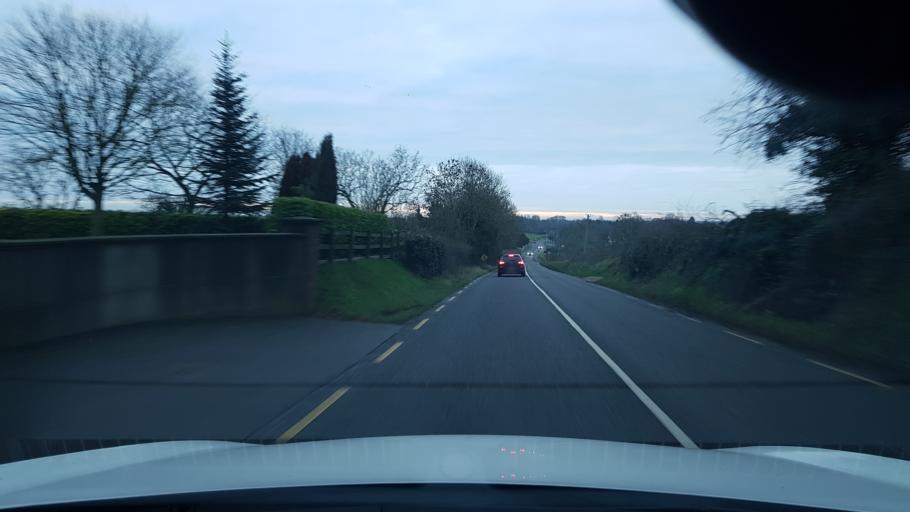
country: IE
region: Leinster
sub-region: An Mhi
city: Navan
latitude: 53.6768
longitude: -6.6759
